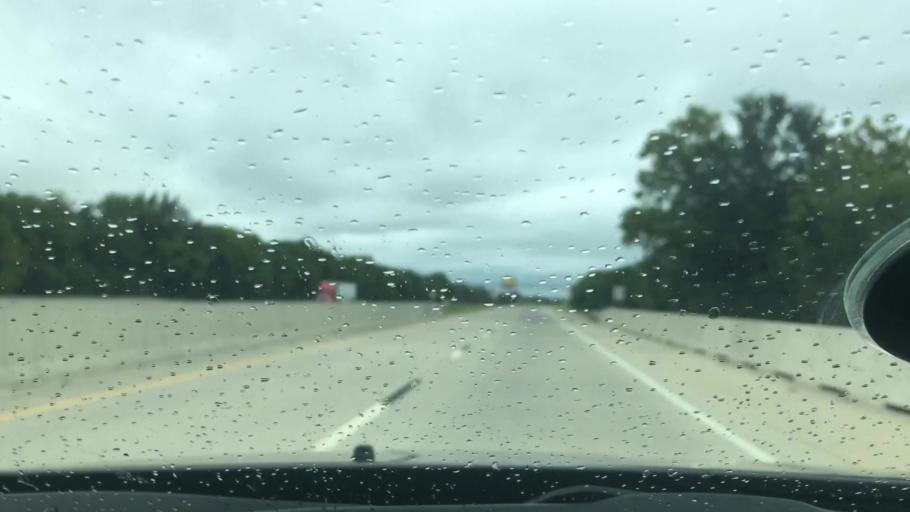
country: US
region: Oklahoma
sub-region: Muskogee County
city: Warner
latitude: 35.4868
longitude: -95.1876
